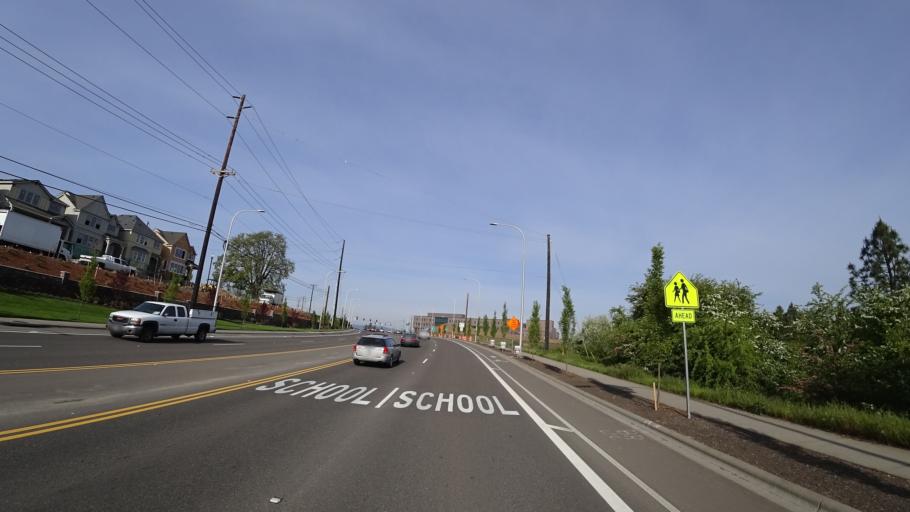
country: US
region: Oregon
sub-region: Washington County
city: King City
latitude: 45.4268
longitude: -122.8505
